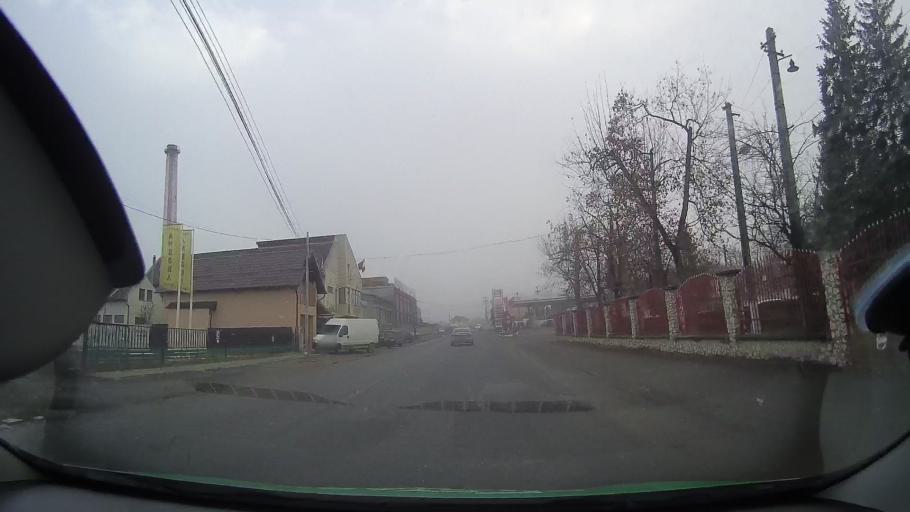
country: RO
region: Mures
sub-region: Municipiul Tarnaveni
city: Tarnaveni
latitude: 46.3165
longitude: 24.2971
